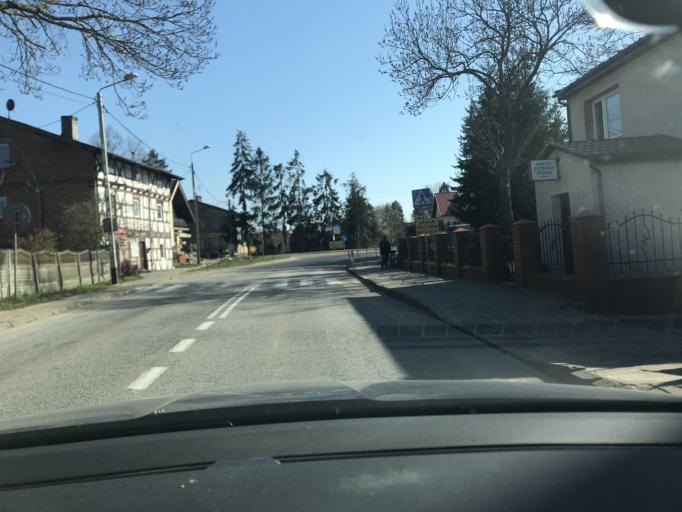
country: PL
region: Pomeranian Voivodeship
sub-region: Powiat nowodworski
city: Sztutowo
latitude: 54.3267
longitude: 19.1790
